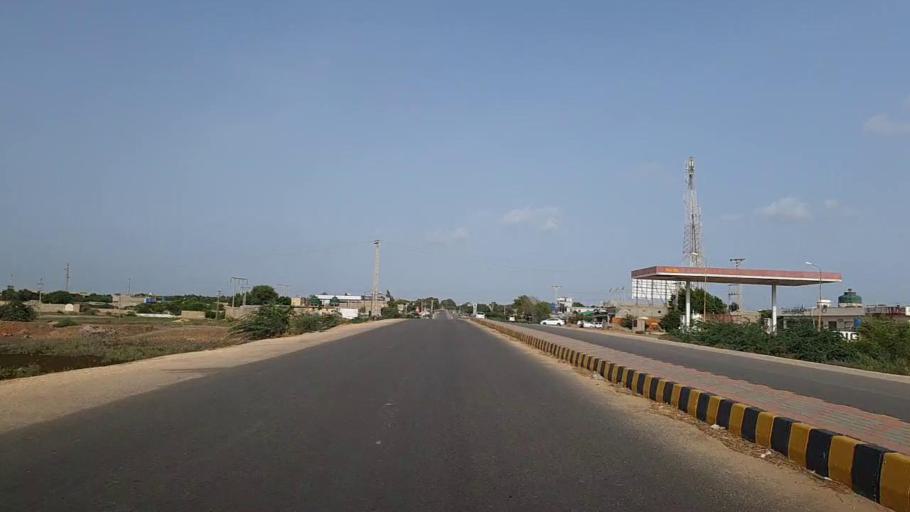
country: PK
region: Sindh
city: Thatta
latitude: 24.7442
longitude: 67.8802
